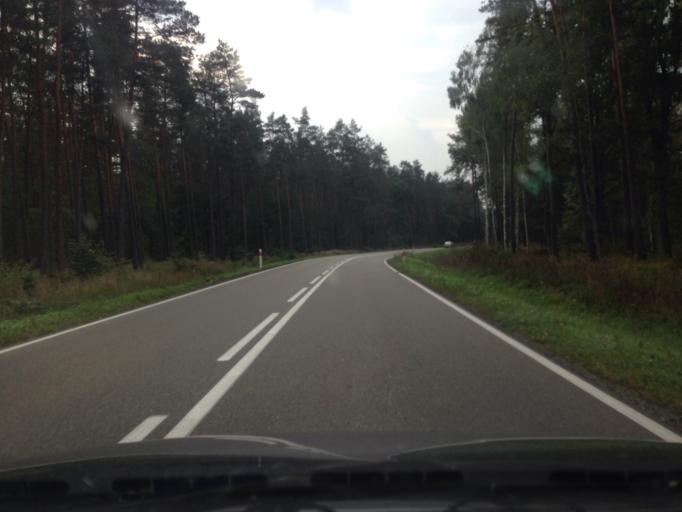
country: PL
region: Pomeranian Voivodeship
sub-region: Powiat kwidzynski
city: Ryjewo
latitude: 53.8274
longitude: 18.9896
